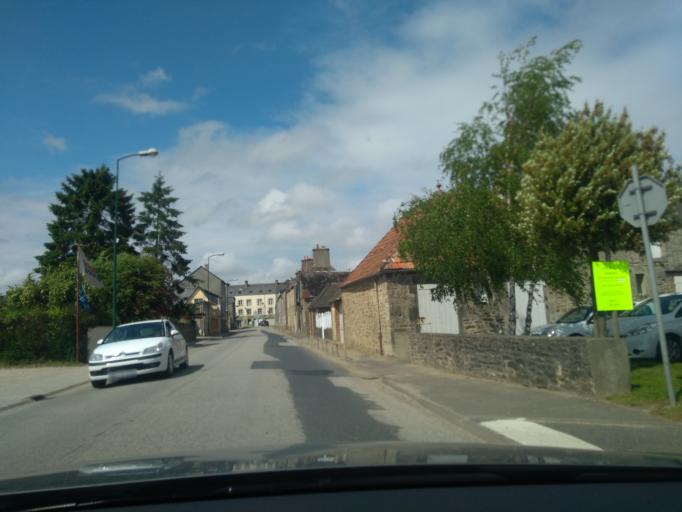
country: FR
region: Lower Normandy
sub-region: Departement de la Manche
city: Quettehou
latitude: 49.5910
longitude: -1.3020
